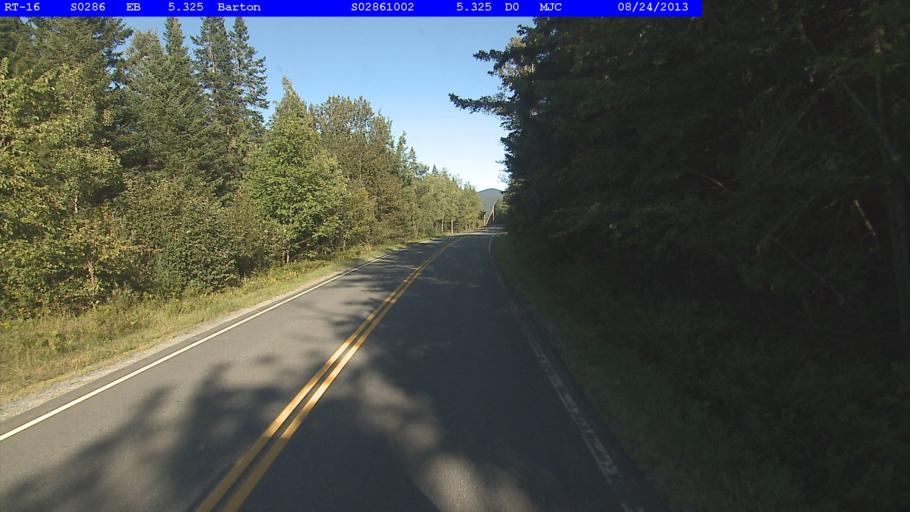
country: US
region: Vermont
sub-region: Orleans County
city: Newport
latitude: 44.7836
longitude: -72.1021
